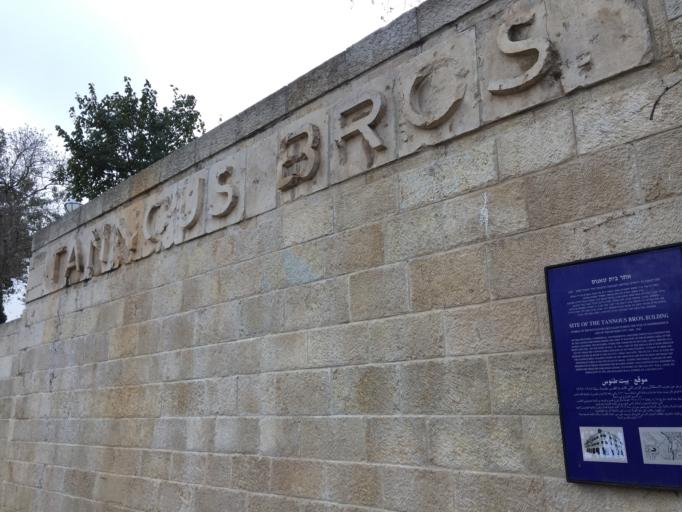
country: PS
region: West Bank
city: Old City
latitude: 31.7758
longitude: 35.2260
